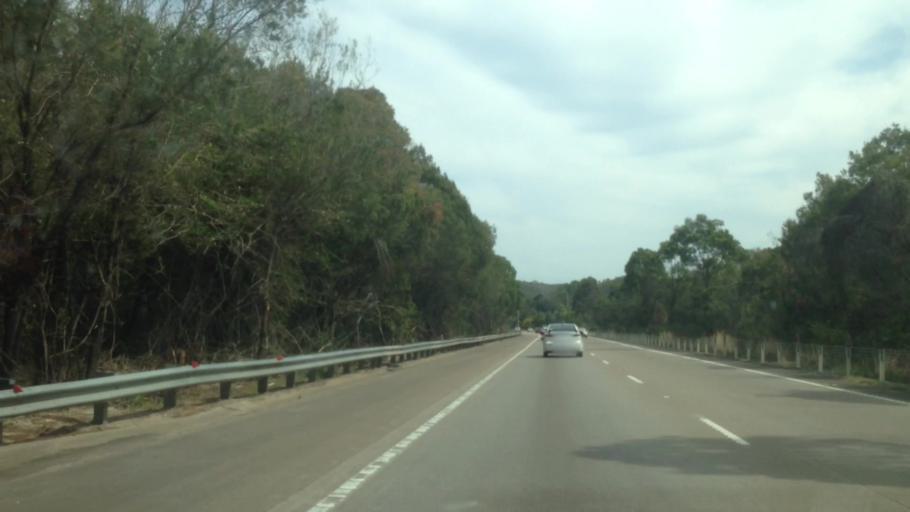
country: AU
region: New South Wales
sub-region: Lake Macquarie Shire
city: Fennell Bay
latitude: -32.9812
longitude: 151.5253
